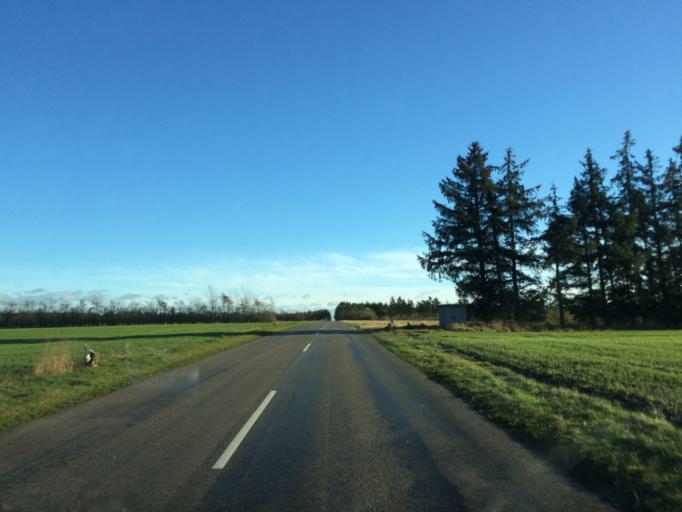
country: DK
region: Central Jutland
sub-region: Ringkobing-Skjern Kommune
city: Videbaek
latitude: 56.0805
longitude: 8.7184
